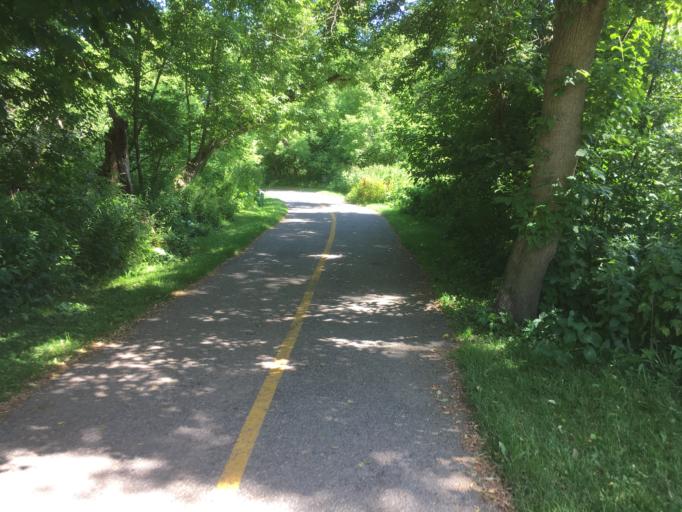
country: CA
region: Ontario
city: Oshawa
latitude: 43.8769
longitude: -78.8565
